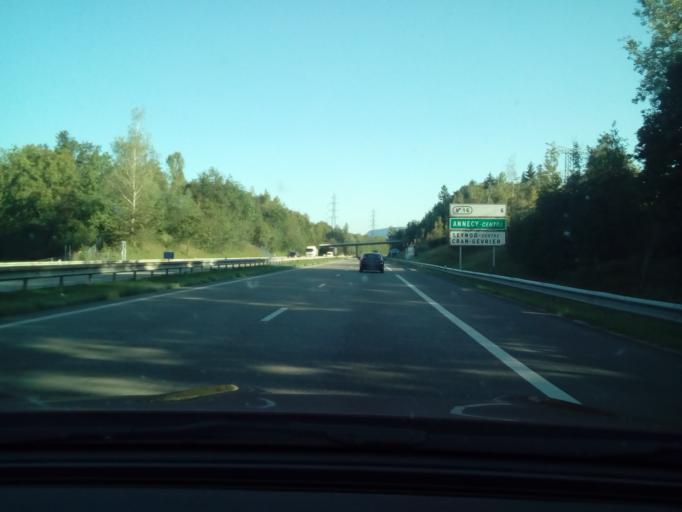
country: FR
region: Rhone-Alpes
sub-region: Departement de la Haute-Savoie
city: Chavanod
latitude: 45.8535
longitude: 6.0566
